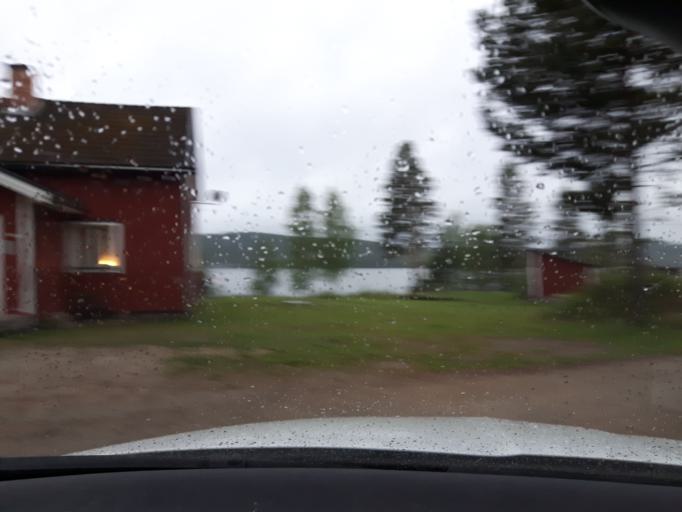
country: SE
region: Gaevleborg
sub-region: Ljusdals Kommun
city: Farila
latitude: 62.0314
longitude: 15.8890
